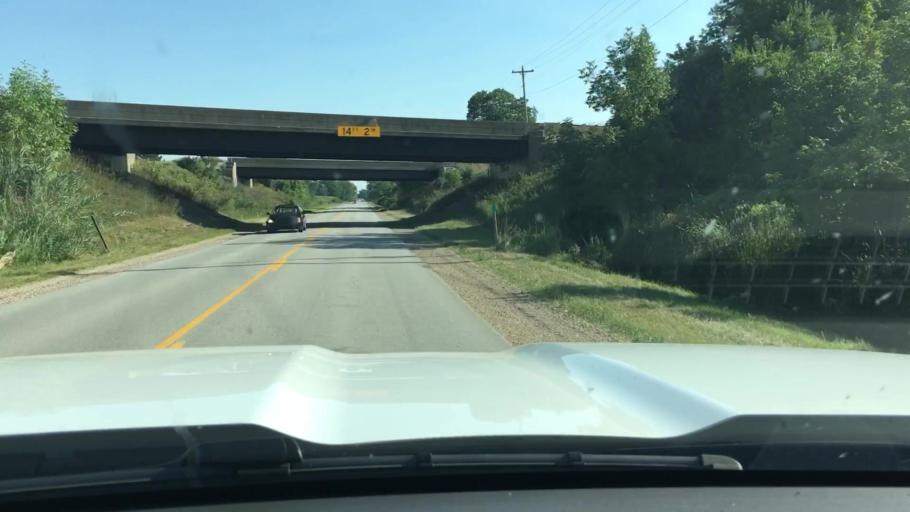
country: US
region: Michigan
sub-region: Ottawa County
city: Zeeland
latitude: 42.8217
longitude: -85.9401
